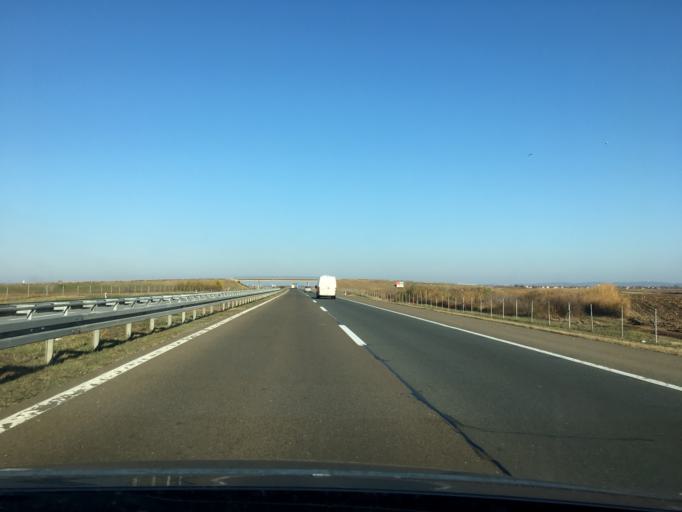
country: RS
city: Novi Karlovci
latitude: 45.0447
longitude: 20.1786
